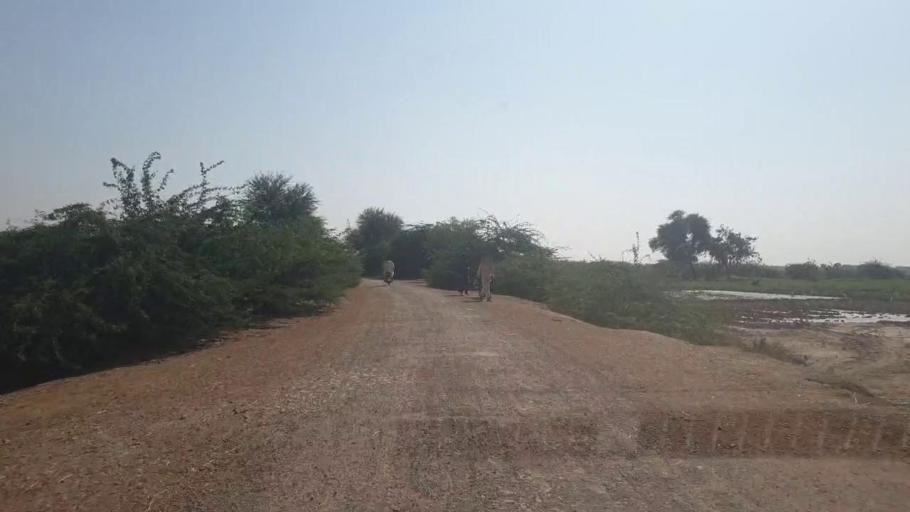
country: PK
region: Sindh
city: Badin
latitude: 24.5564
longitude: 68.8457
